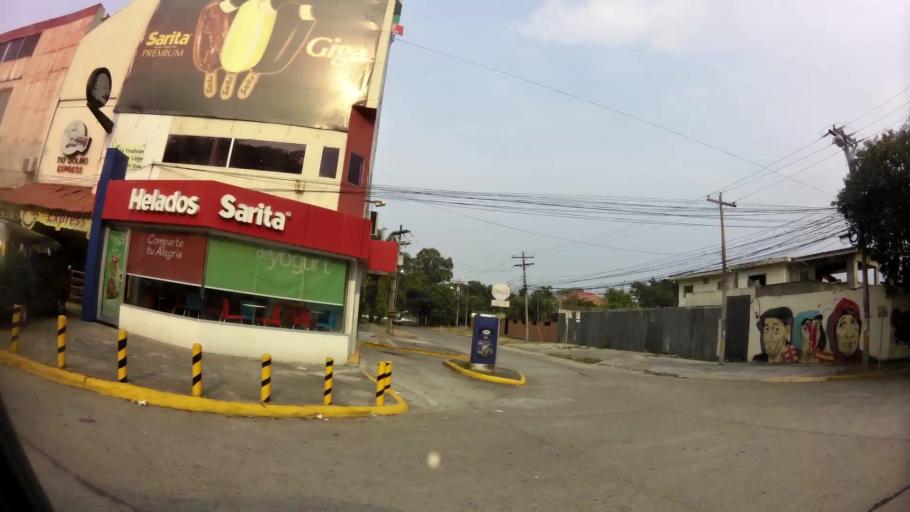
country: HN
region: Cortes
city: San Pedro Sula
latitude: 15.5161
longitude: -88.0311
